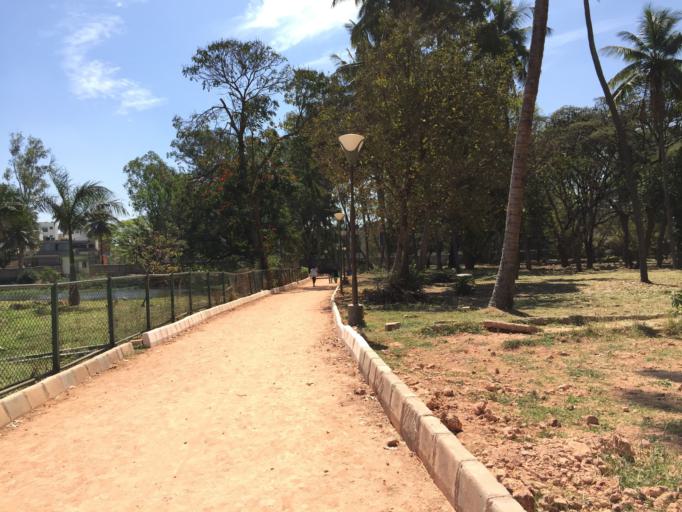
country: IN
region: Karnataka
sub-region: Bangalore Urban
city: Bangalore
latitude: 12.9449
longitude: 77.5814
